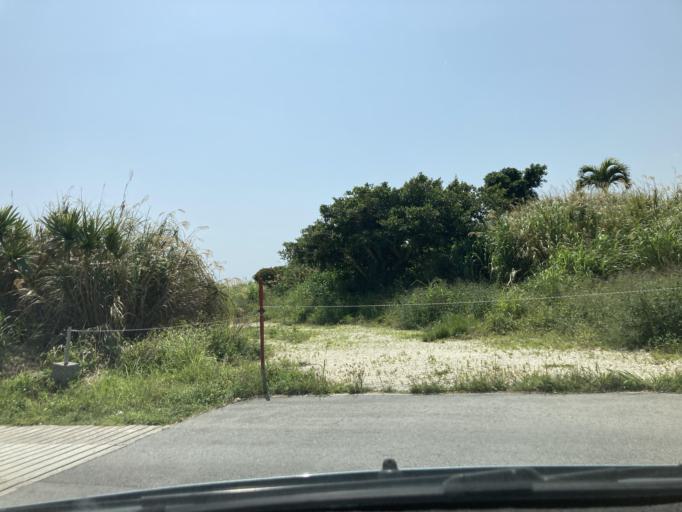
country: JP
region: Okinawa
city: Ginowan
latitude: 26.1622
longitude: 127.8113
